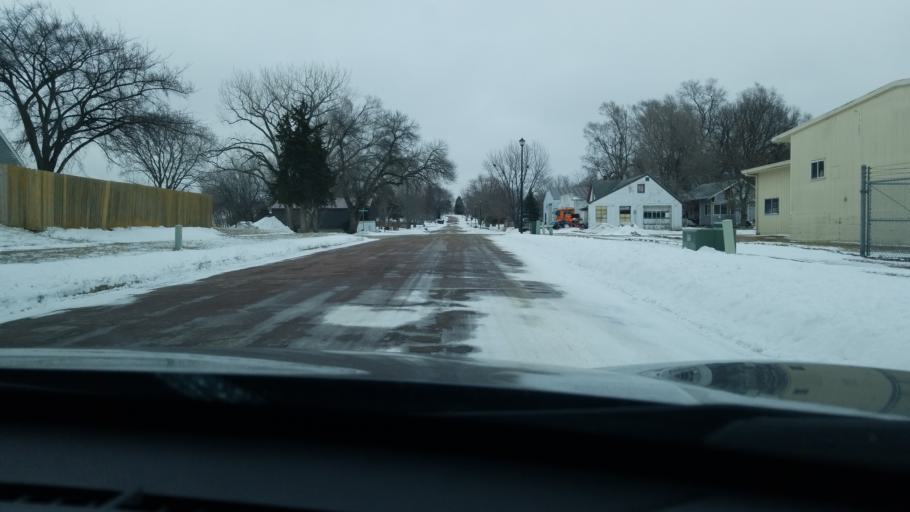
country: US
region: Iowa
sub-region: Lyon County
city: Rock Rapids
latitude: 43.4321
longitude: -96.1614
